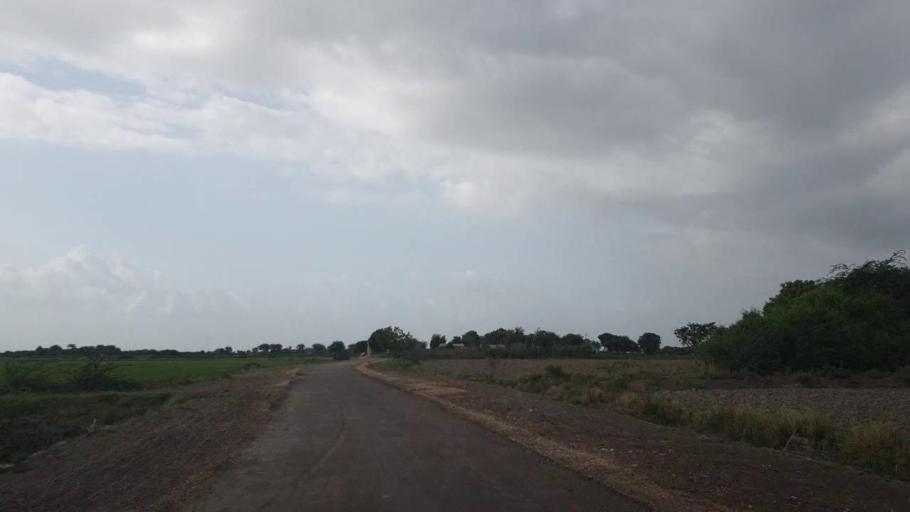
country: PK
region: Sindh
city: Kadhan
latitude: 24.5995
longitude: 69.0565
